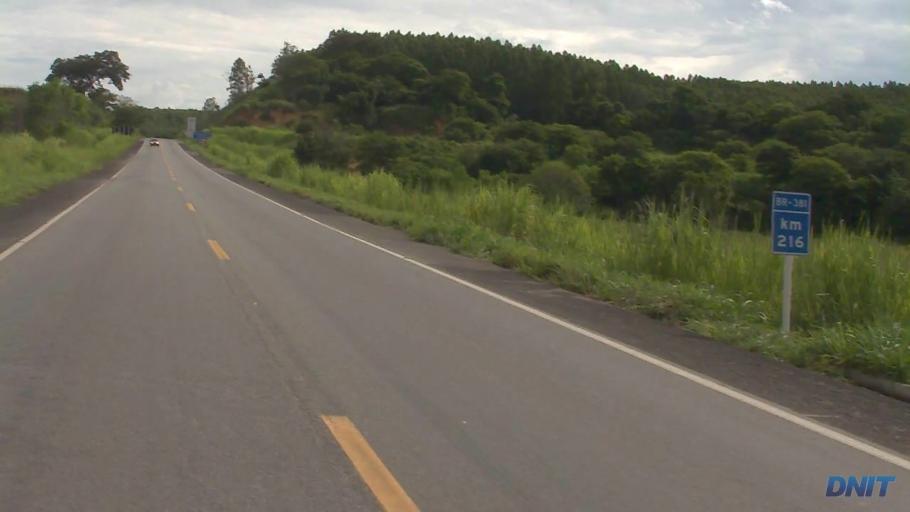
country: BR
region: Minas Gerais
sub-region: Belo Oriente
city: Belo Oriente
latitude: -19.2436
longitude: -42.3363
